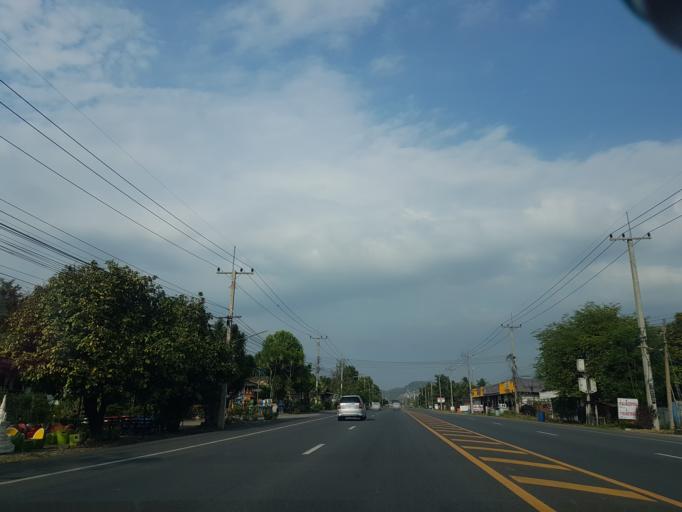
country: TH
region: Sara Buri
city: Ban Mo
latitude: 14.6567
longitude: 100.7647
